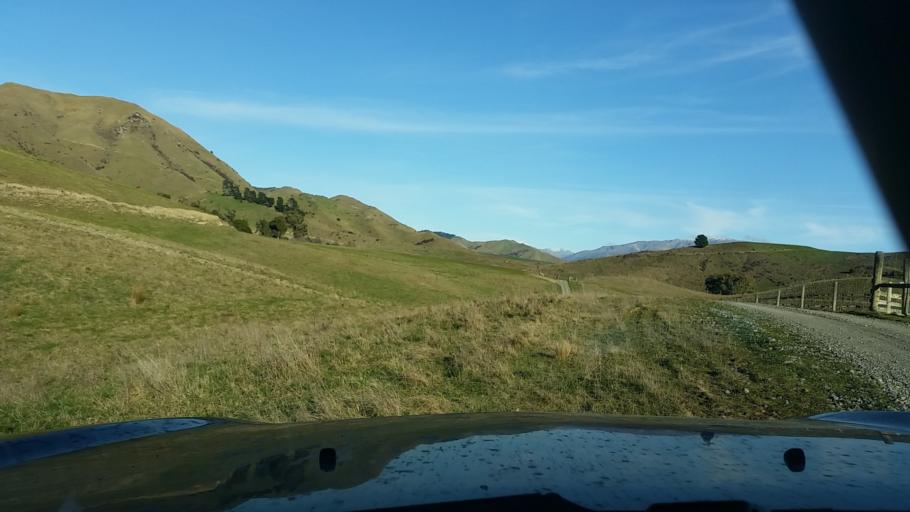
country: NZ
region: Marlborough
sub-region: Marlborough District
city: Blenheim
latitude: -41.7361
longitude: 173.9910
